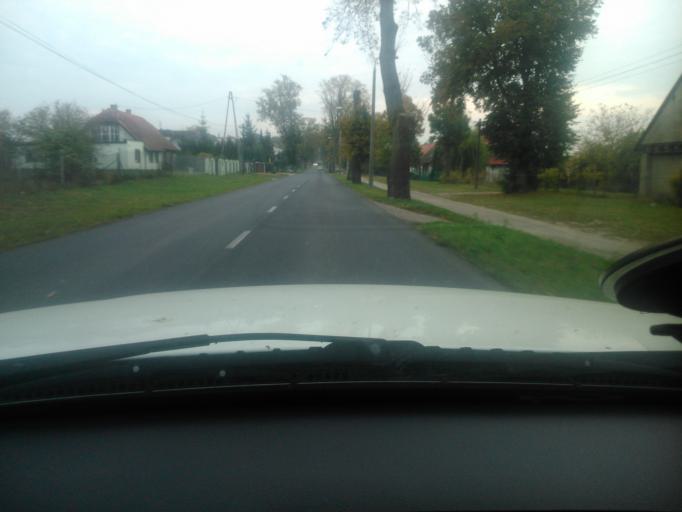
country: PL
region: Kujawsko-Pomorskie
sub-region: Powiat golubsko-dobrzynski
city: Kowalewo Pomorskie
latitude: 53.1583
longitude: 18.8855
